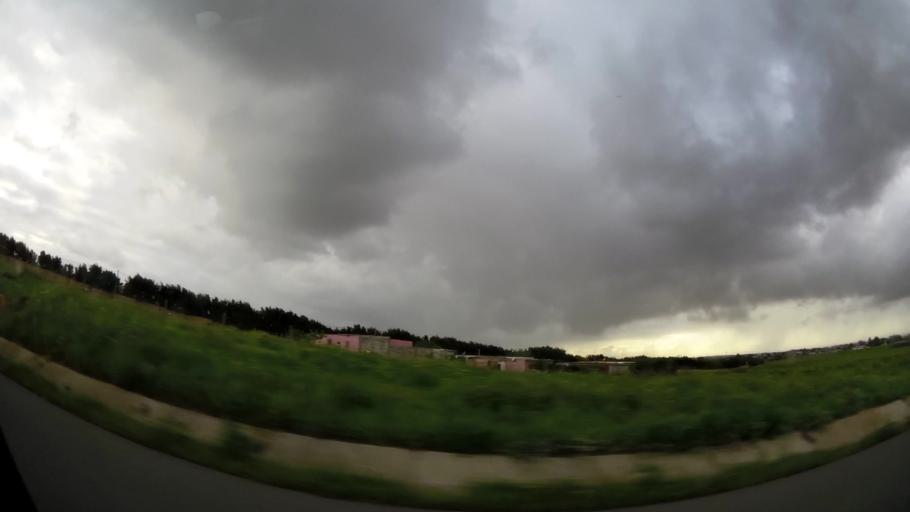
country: MA
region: Grand Casablanca
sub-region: Mediouna
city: Tit Mellil
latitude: 33.5791
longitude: -7.4532
